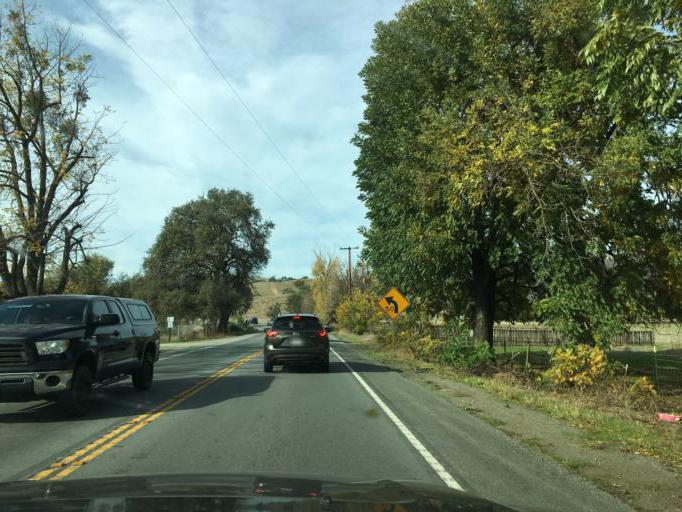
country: US
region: California
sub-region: Santa Clara County
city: Gilroy
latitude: 36.9839
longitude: -121.4404
